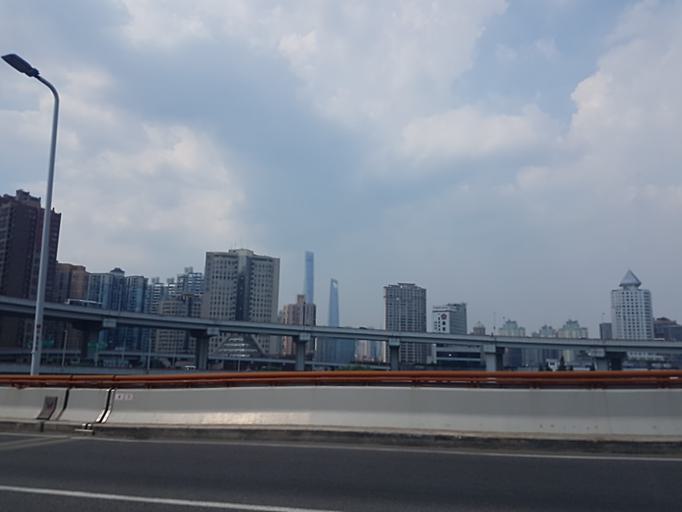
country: CN
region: Shanghai Shi
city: Luwan
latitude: 31.2094
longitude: 121.4970
